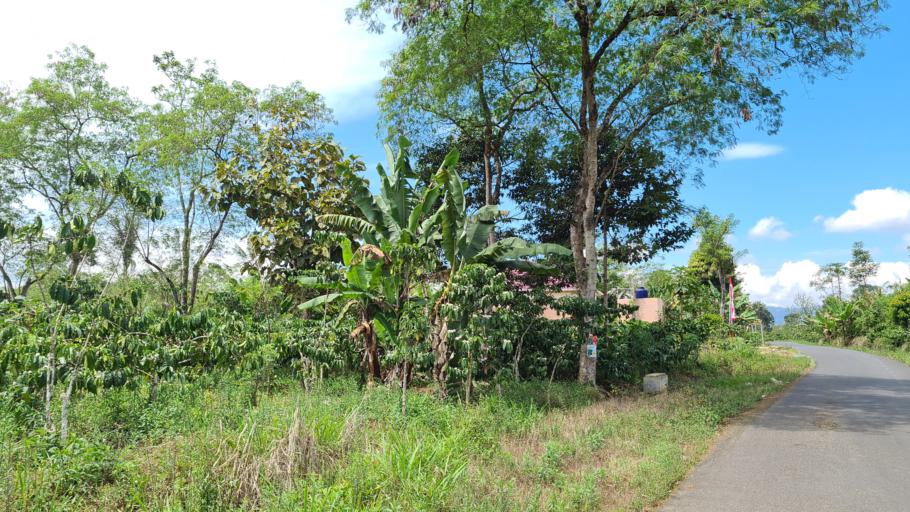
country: ID
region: Lampung
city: Kenali
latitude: -5.0956
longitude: 104.4318
